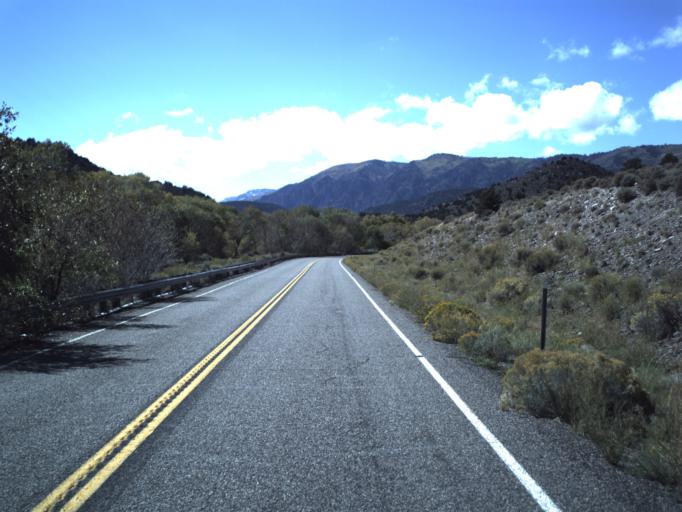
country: US
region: Utah
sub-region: Piute County
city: Junction
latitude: 38.2589
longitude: -112.2643
